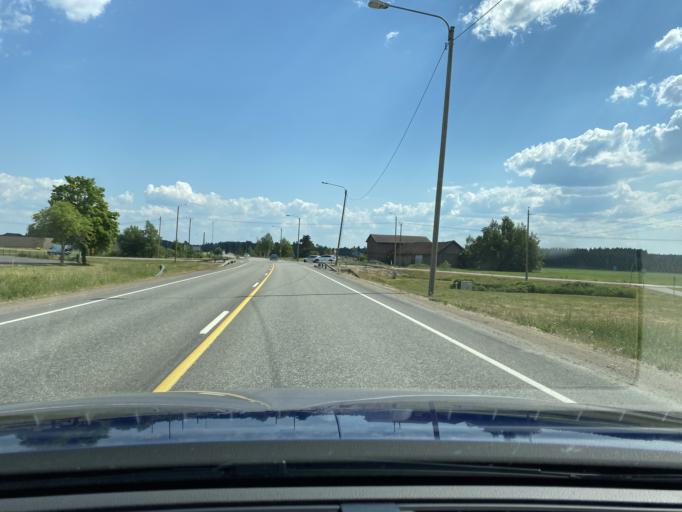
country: FI
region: Satakunta
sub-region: Rauma
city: Eura
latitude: 61.1244
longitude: 22.1293
